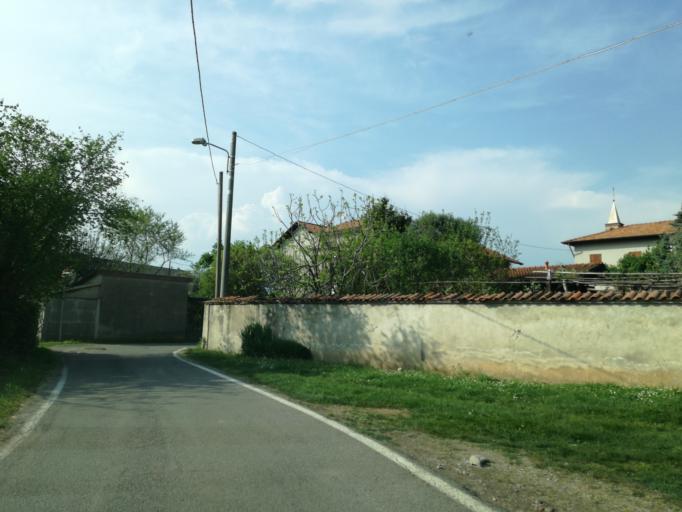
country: IT
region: Lombardy
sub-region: Provincia di Lecco
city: Verderio Superiore
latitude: 45.6600
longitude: 9.4471
